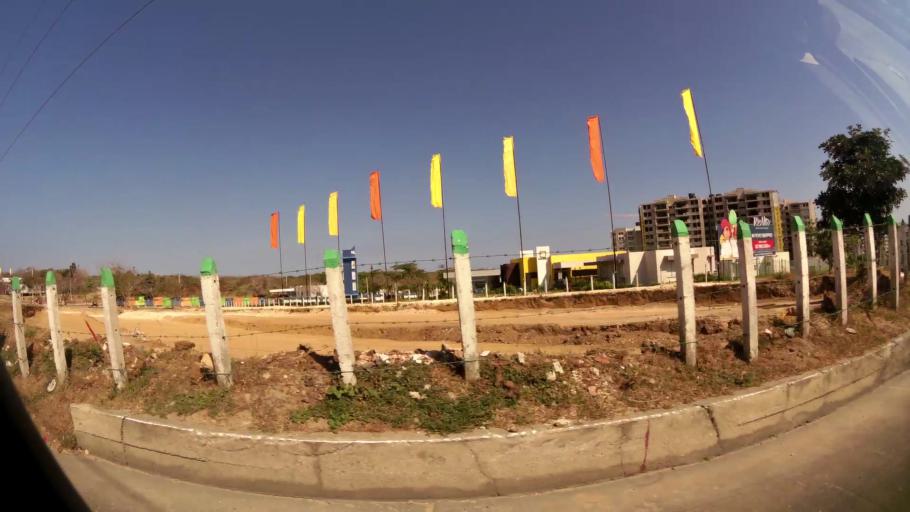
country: CO
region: Atlantico
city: Barranquilla
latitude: 11.0199
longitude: -74.8203
